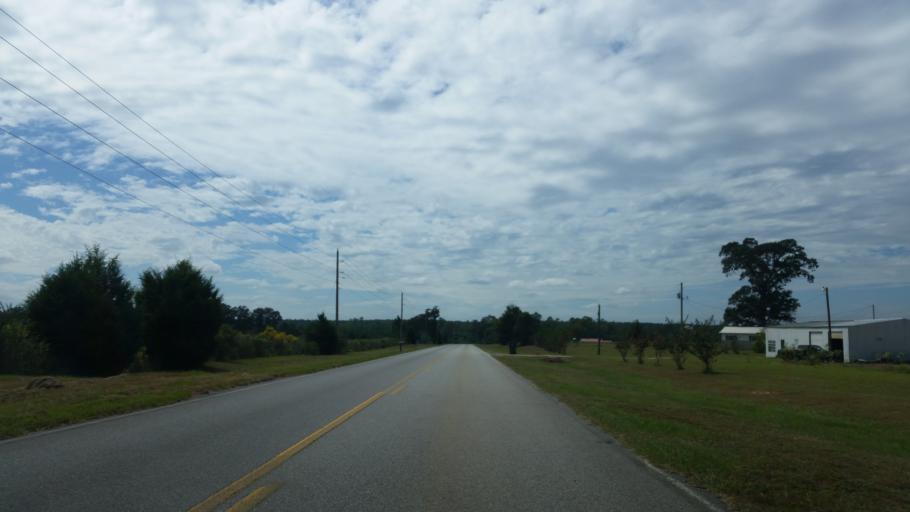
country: US
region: Florida
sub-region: Santa Rosa County
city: Point Baker
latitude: 30.8384
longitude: -86.8955
